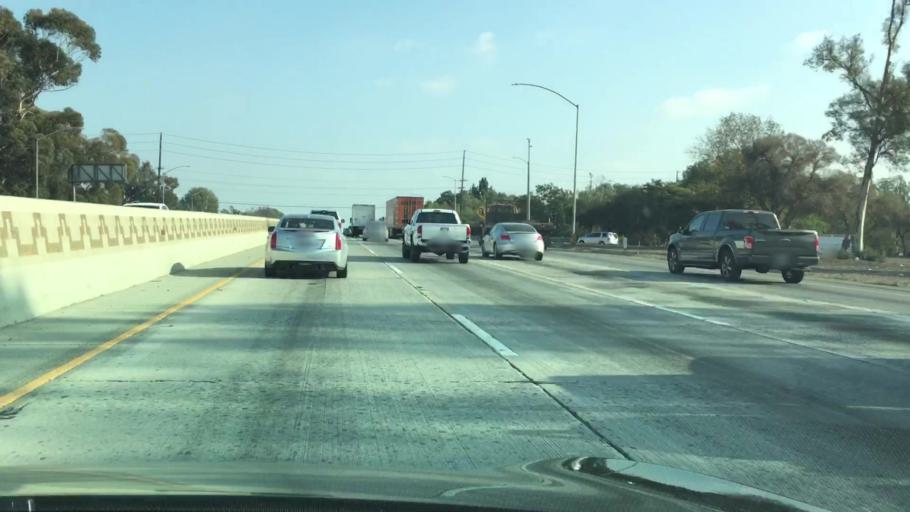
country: US
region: California
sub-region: Los Angeles County
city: Downey
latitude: 33.9588
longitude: -118.1131
